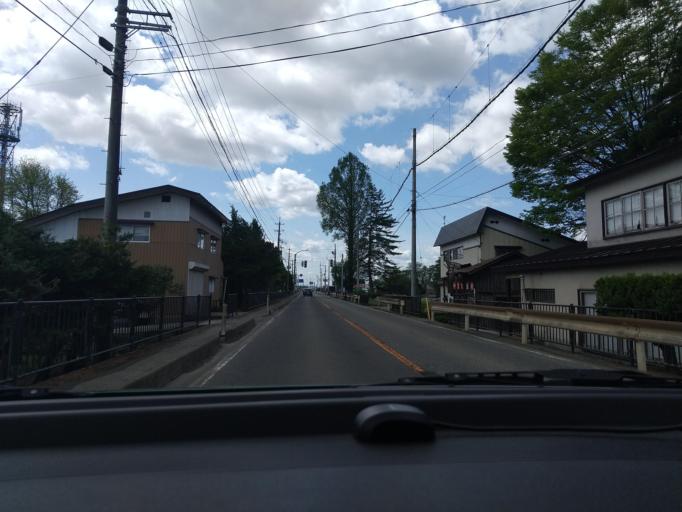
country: JP
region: Akita
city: Kakunodatemachi
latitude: 39.5711
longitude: 140.5617
